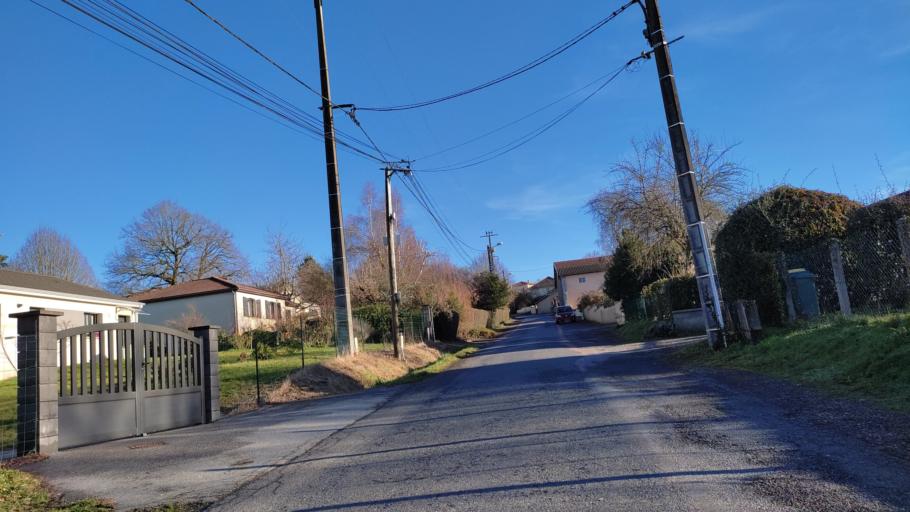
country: FR
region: Limousin
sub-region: Departement de la Haute-Vienne
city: Isle
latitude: 45.8096
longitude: 1.1968
